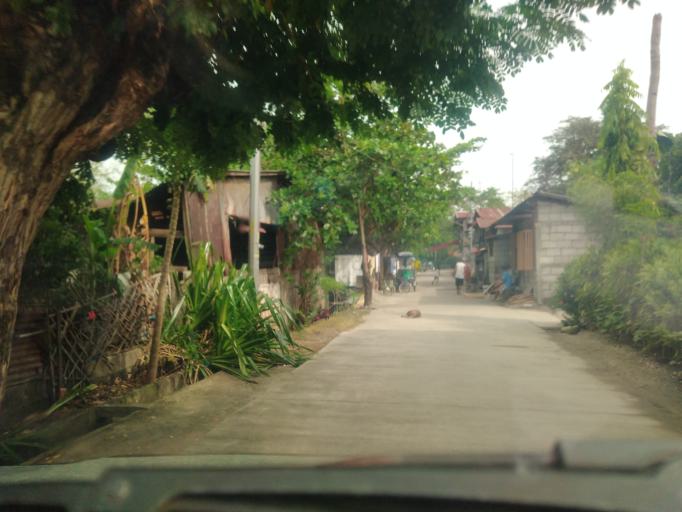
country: PH
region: Central Luzon
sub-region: Province of Pampanga
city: Pau
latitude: 15.0110
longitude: 120.7128
